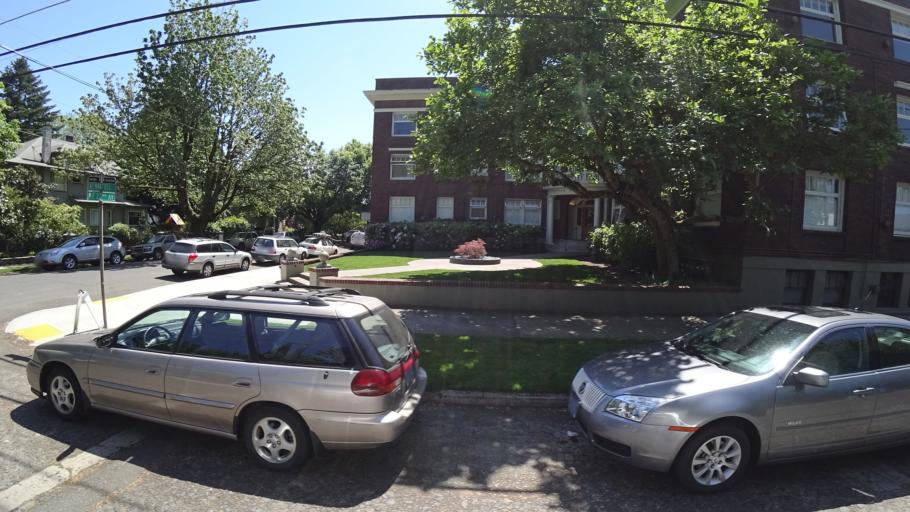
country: US
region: Oregon
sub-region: Multnomah County
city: Portland
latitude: 45.5365
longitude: -122.6432
